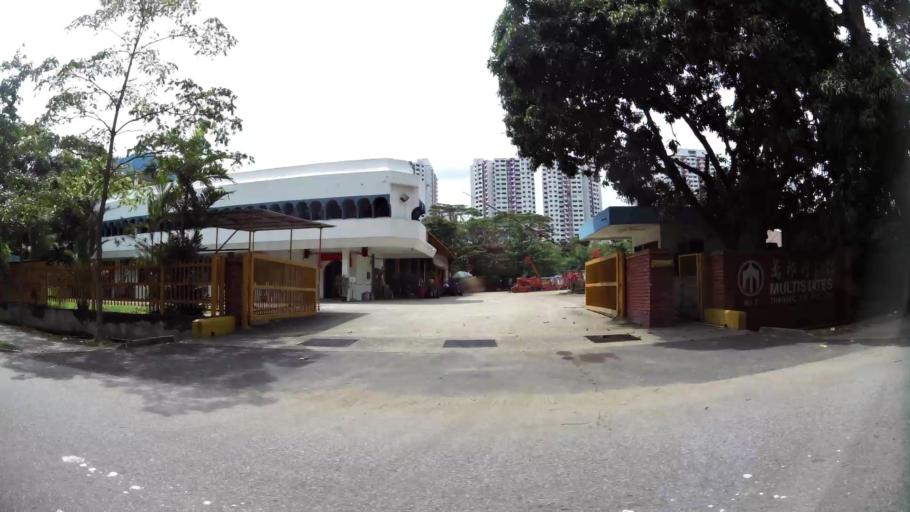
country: MY
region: Johor
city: Johor Bahru
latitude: 1.4005
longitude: 103.7540
